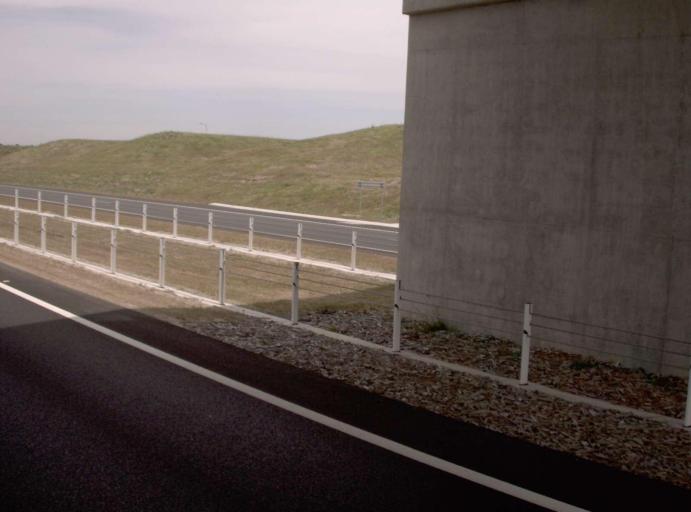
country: AU
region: Victoria
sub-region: Mornington Peninsula
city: Moorooduc
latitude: -38.2330
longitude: 145.1253
